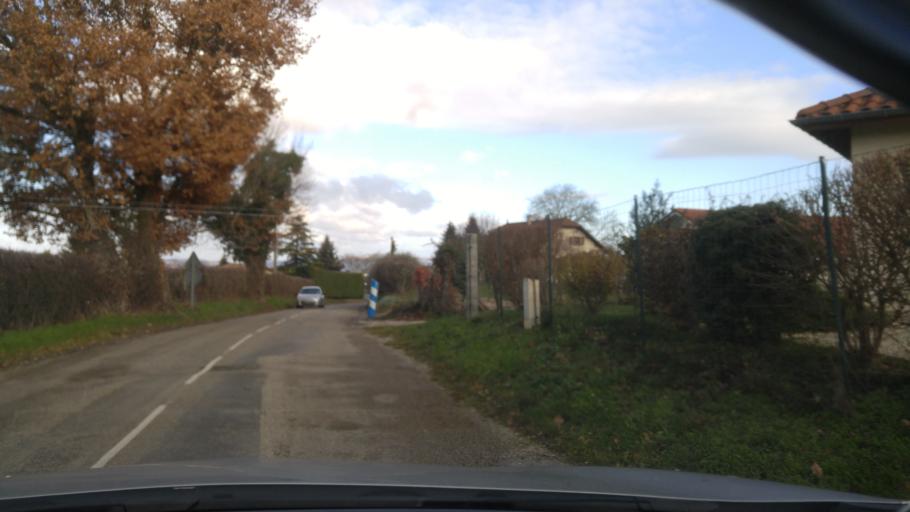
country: FR
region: Rhone-Alpes
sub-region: Departement de l'Isere
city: Roche
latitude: 45.5703
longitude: 5.1870
